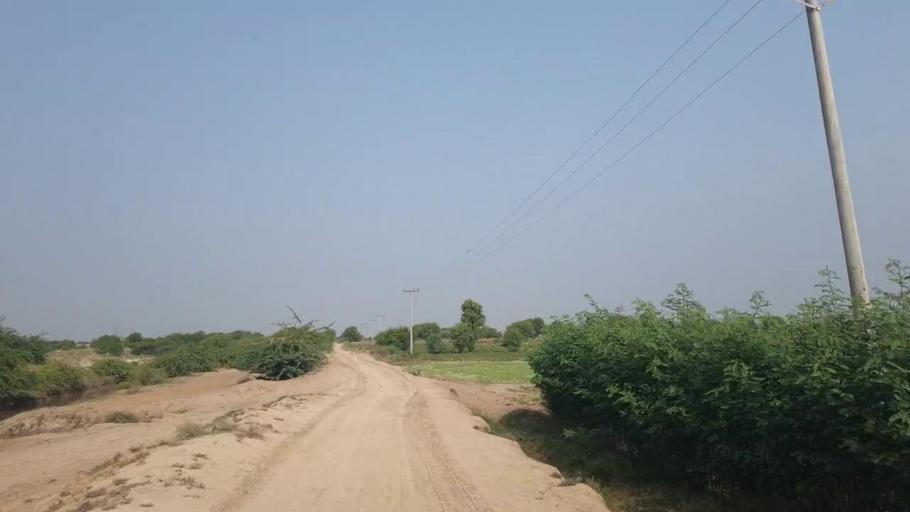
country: PK
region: Sindh
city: Badin
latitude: 24.6964
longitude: 68.7784
